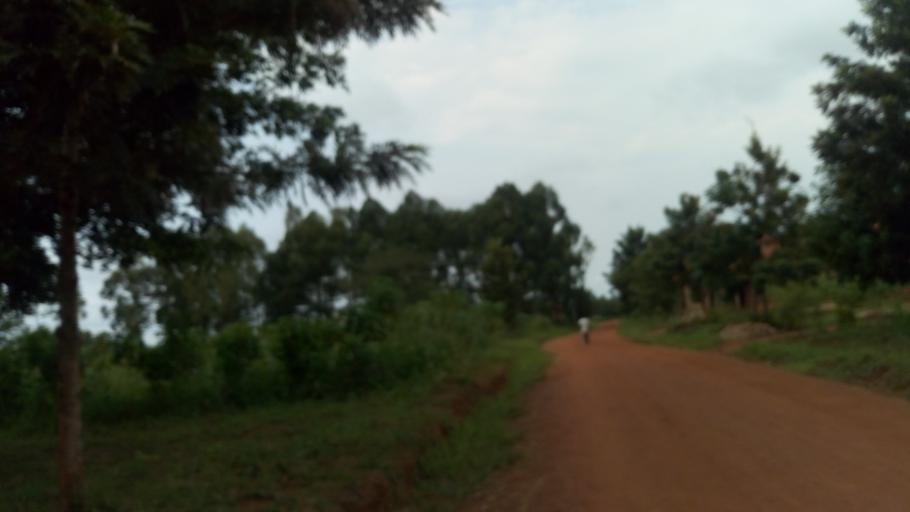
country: UG
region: Western Region
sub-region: Kiryandongo District
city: Kiryandongo
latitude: 1.8001
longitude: 32.0084
